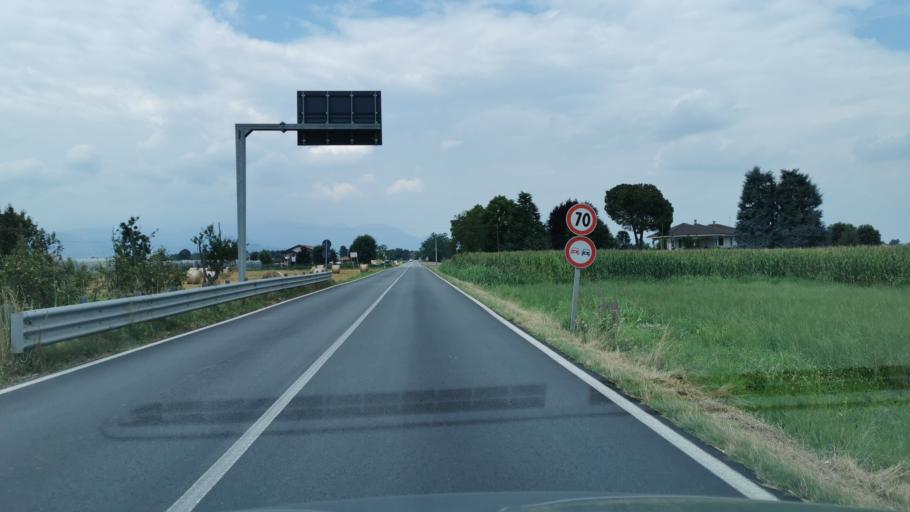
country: IT
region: Piedmont
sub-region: Provincia di Torino
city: Garzigliana
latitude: 44.8180
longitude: 7.3710
